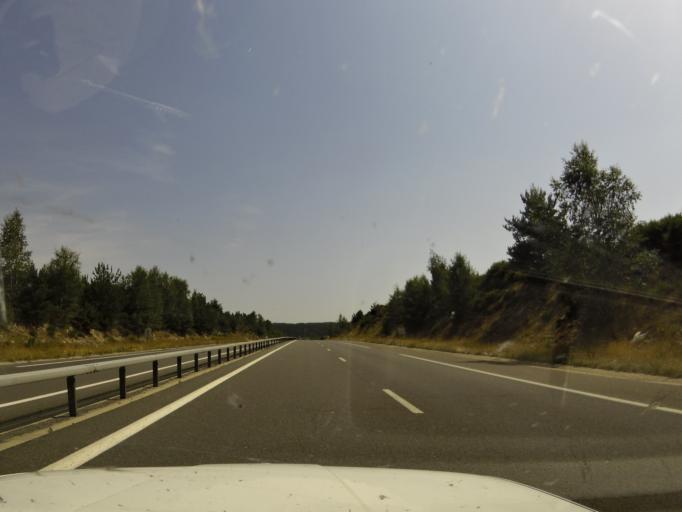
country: FR
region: Languedoc-Roussillon
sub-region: Departement de la Lozere
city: Le Malzieu-Ville
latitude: 44.8007
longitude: 3.2936
